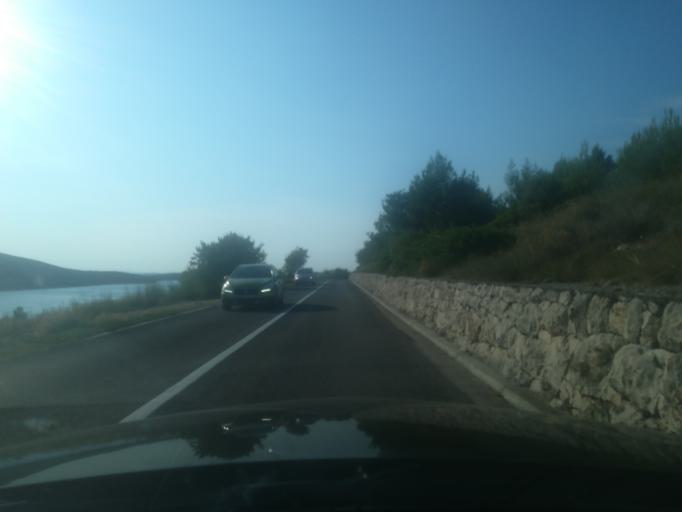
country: HR
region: Primorsko-Goranska
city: Banjol
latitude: 44.7117
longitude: 14.8294
